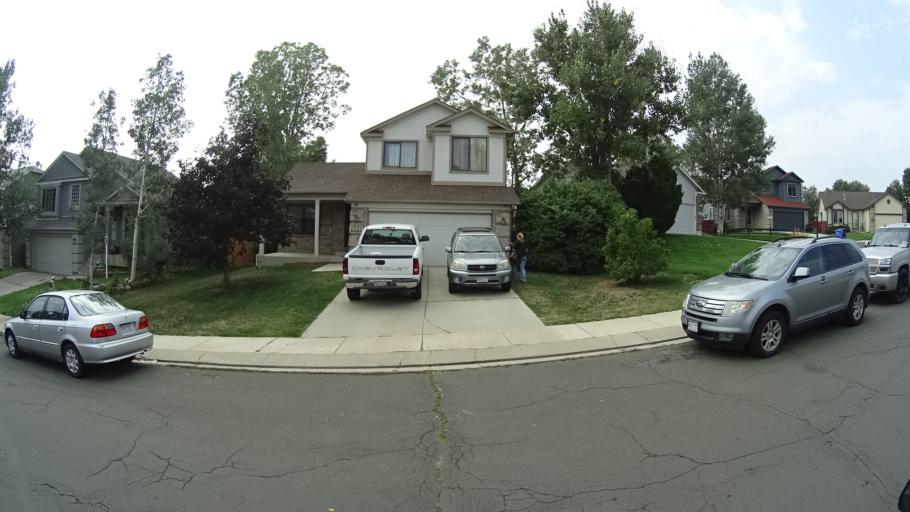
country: US
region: Colorado
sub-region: El Paso County
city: Stratmoor
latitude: 38.8218
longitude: -104.7469
